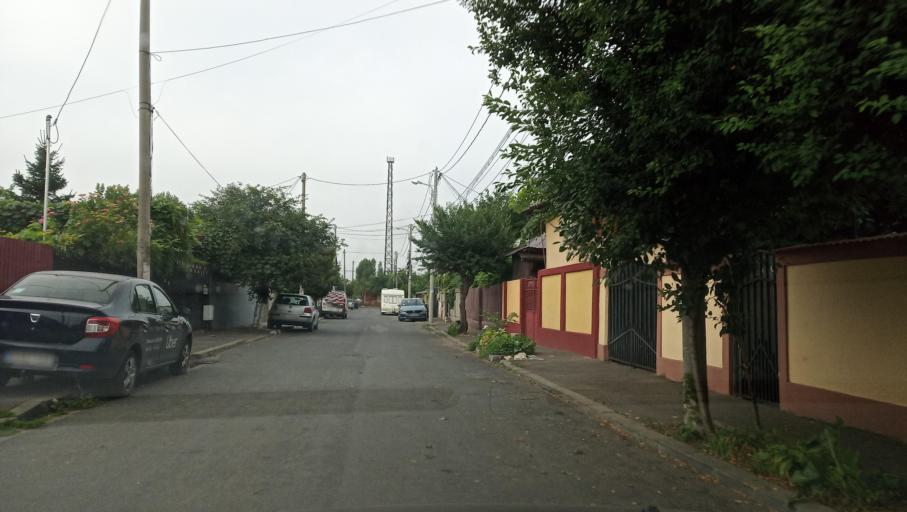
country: RO
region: Ilfov
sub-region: Comuna Pantelimon
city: Pantelimon
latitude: 44.4262
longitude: 26.2078
